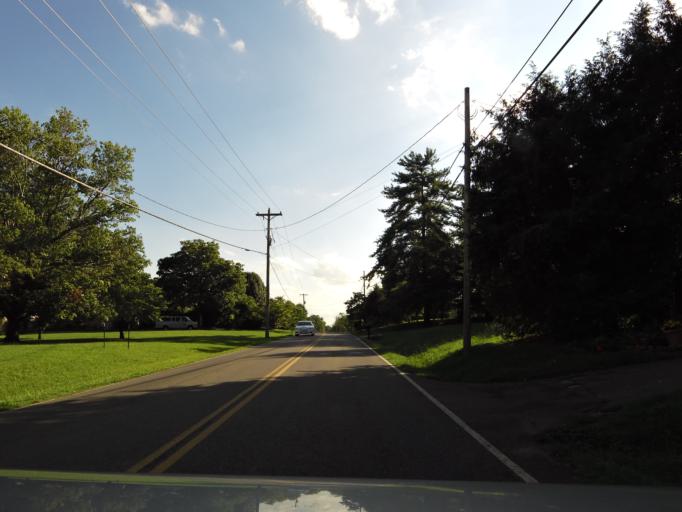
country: US
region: Tennessee
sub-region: Blount County
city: Maryville
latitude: 35.7025
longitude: -84.0233
